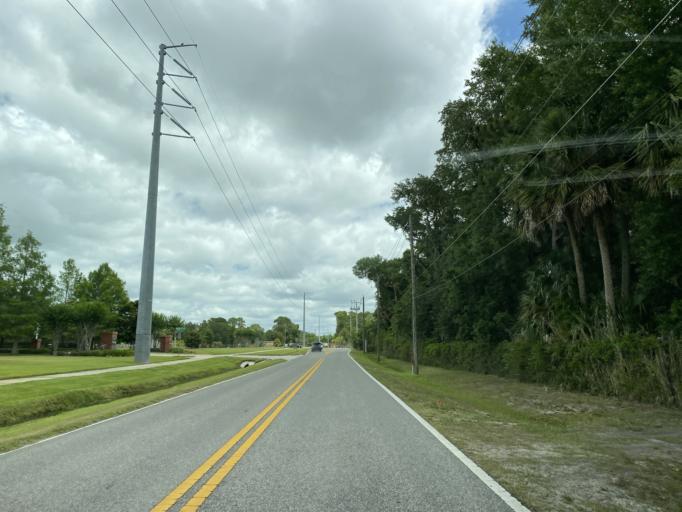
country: US
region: Florida
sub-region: Volusia County
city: DeBary
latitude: 28.8262
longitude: -81.3392
